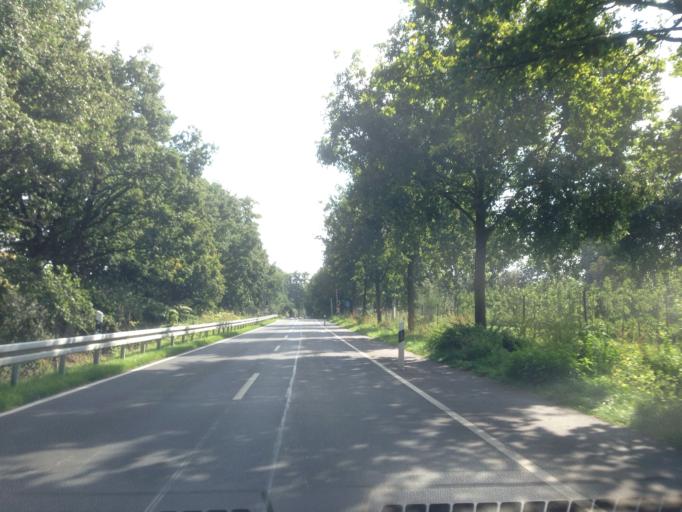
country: DE
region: North Rhine-Westphalia
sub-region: Regierungsbezirk Munster
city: Muenster
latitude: 52.0074
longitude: 7.6110
